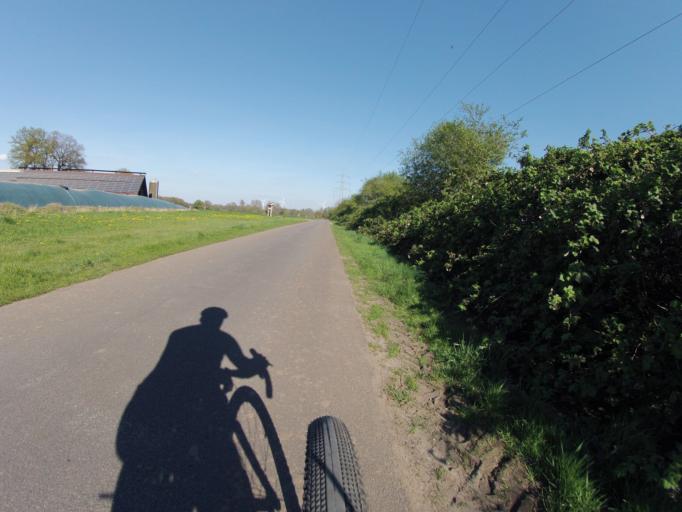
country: DE
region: Lower Saxony
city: Quendorf
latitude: 52.3448
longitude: 7.1722
